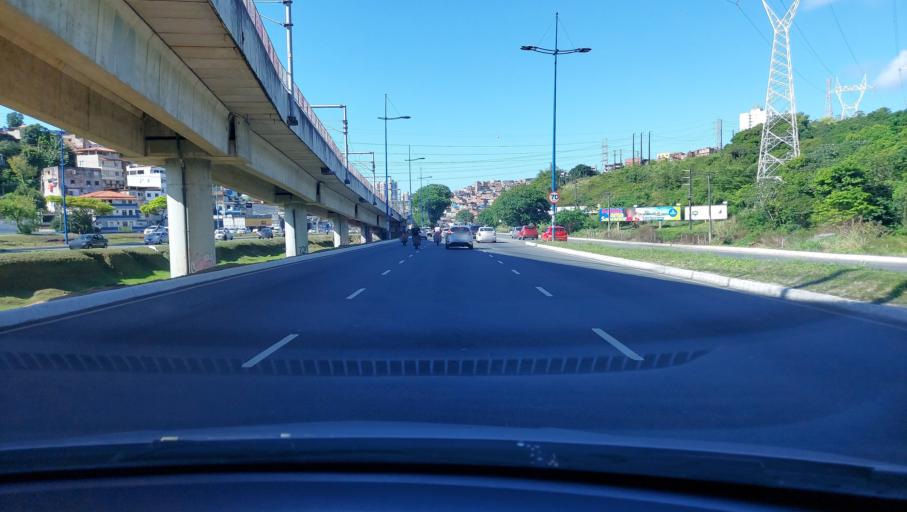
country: BR
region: Bahia
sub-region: Salvador
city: Salvador
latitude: -12.9761
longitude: -38.4783
